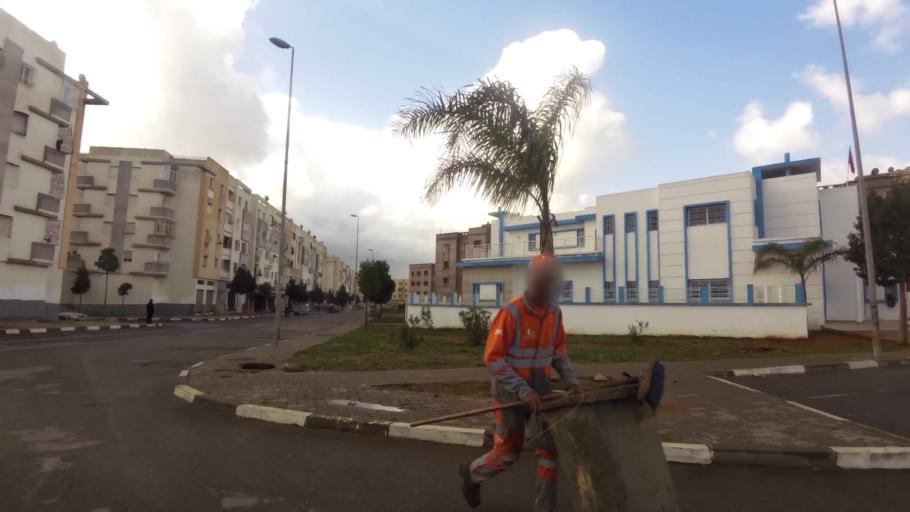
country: MA
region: Grand Casablanca
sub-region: Nouaceur
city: Bouskoura
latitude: 33.5381
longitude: -7.7040
